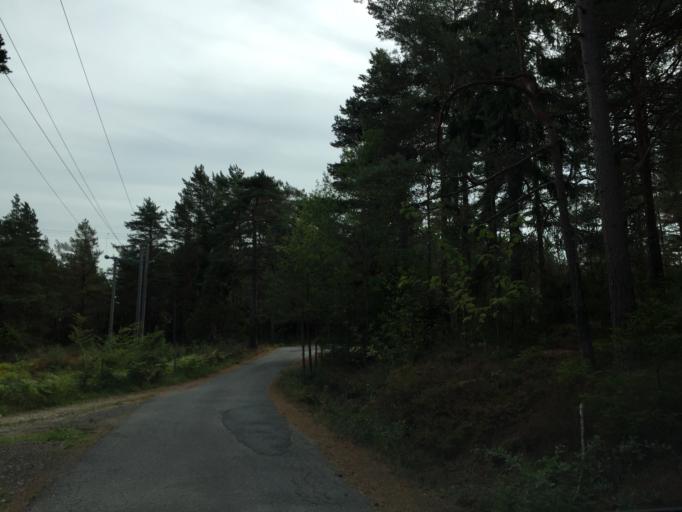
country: NO
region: Ostfold
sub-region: Fredrikstad
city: Fredrikstad
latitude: 59.0997
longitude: 10.9357
